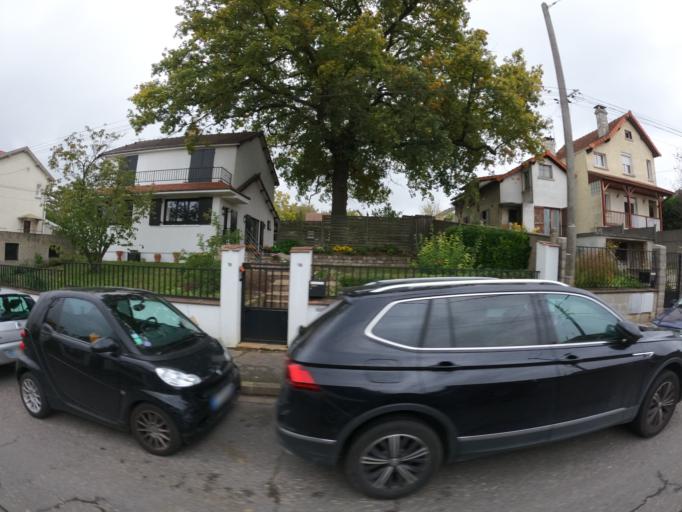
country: FR
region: Ile-de-France
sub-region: Departement du Val-de-Marne
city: Sucy-en-Brie
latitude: 48.7799
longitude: 2.5217
